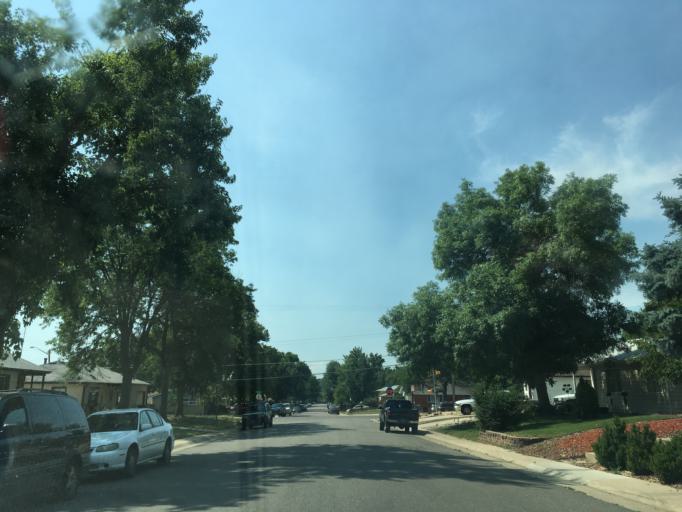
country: US
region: Colorado
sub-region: Jefferson County
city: Lakewood
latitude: 39.6903
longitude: -105.0453
